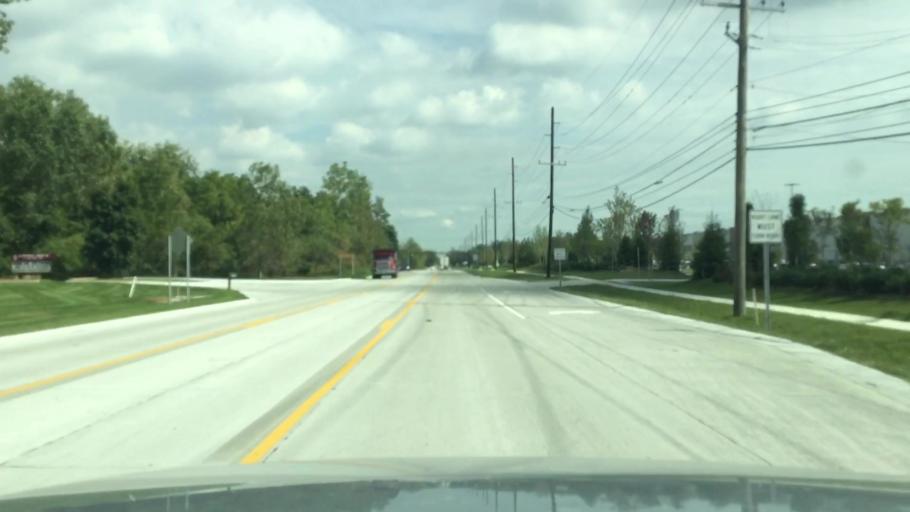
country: US
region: Michigan
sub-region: Wayne County
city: Wayne
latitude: 42.2524
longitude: -83.3655
